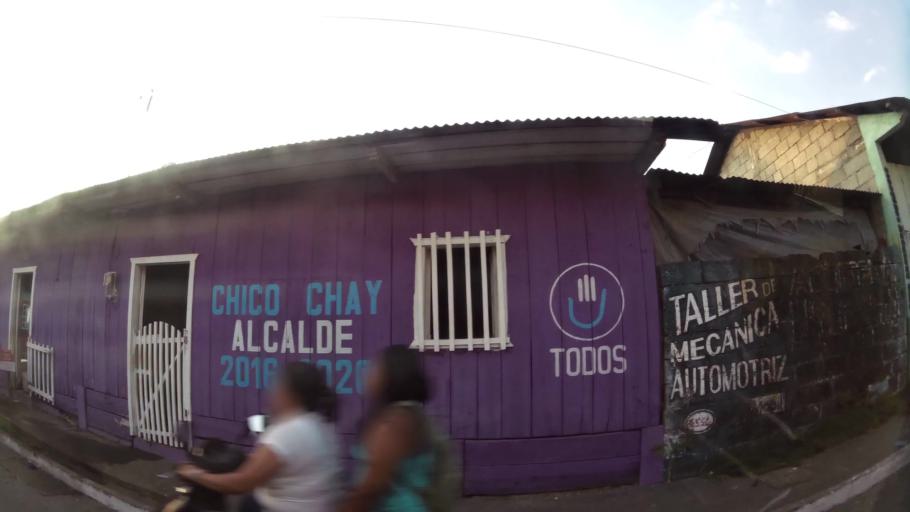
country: GT
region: Retalhuleu
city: San Sebastian
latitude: 14.5611
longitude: -91.6509
